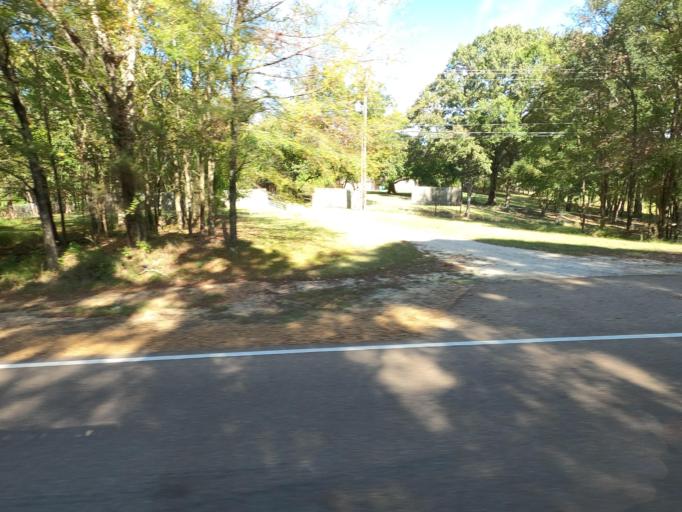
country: US
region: Tennessee
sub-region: Shelby County
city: Arlington
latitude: 35.2495
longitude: -89.6508
